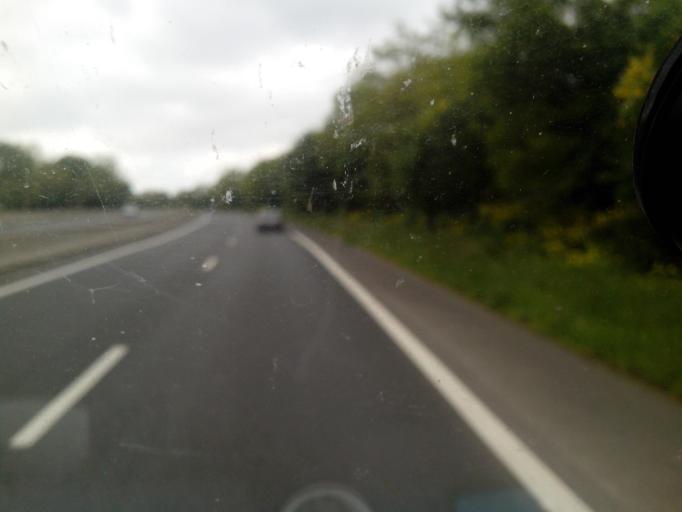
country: FR
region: Lower Normandy
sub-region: Departement du Calvados
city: Mathieu
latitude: 49.2464
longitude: -0.3728
